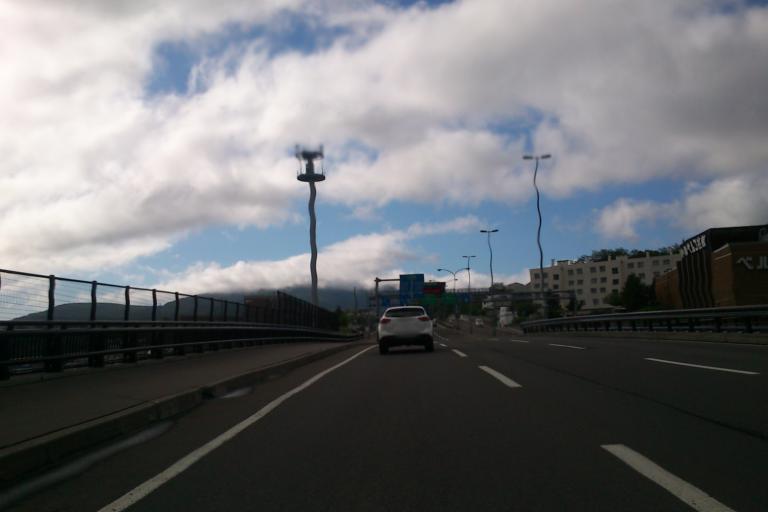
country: JP
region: Hokkaido
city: Otaru
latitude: 43.1834
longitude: 141.0181
